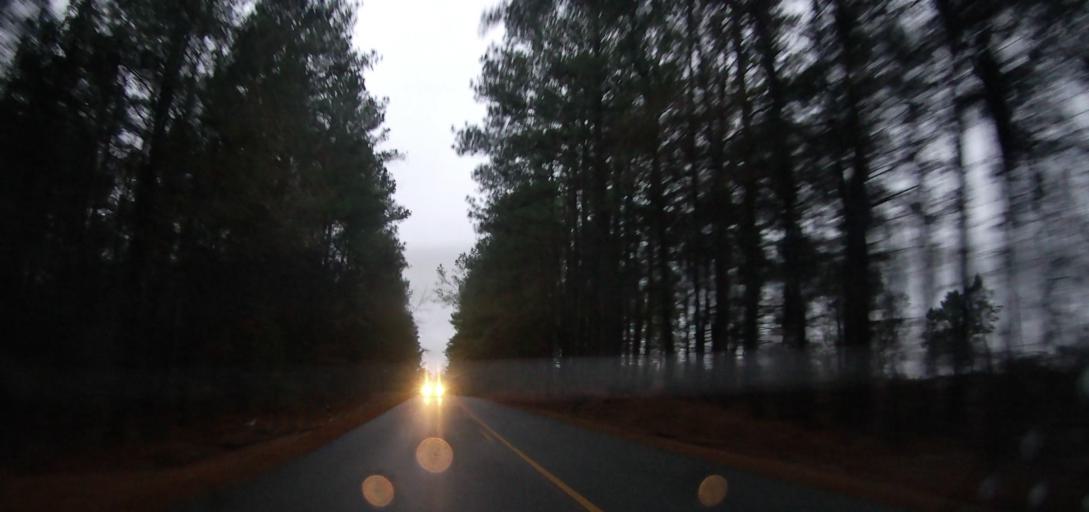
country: US
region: Alabama
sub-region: Tuscaloosa County
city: Vance
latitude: 33.1378
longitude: -87.2297
